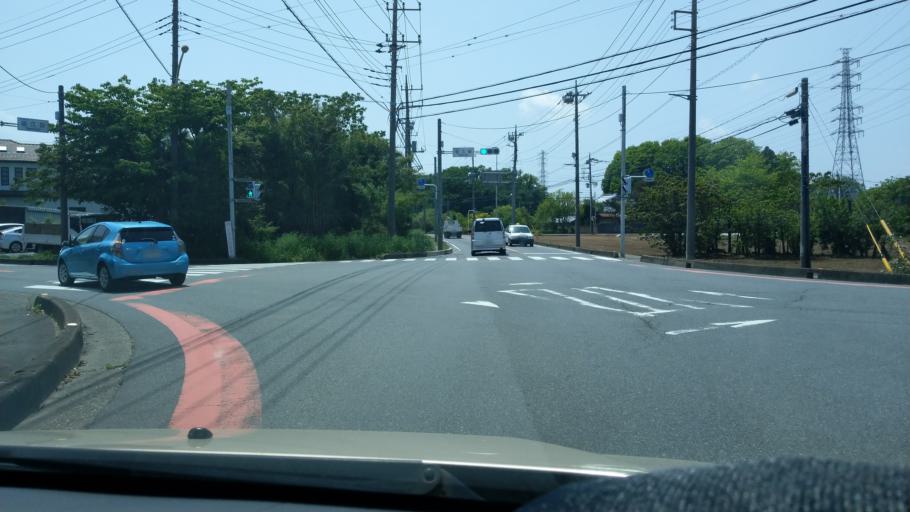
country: JP
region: Saitama
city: Iwatsuki
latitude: 35.9206
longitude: 139.7184
